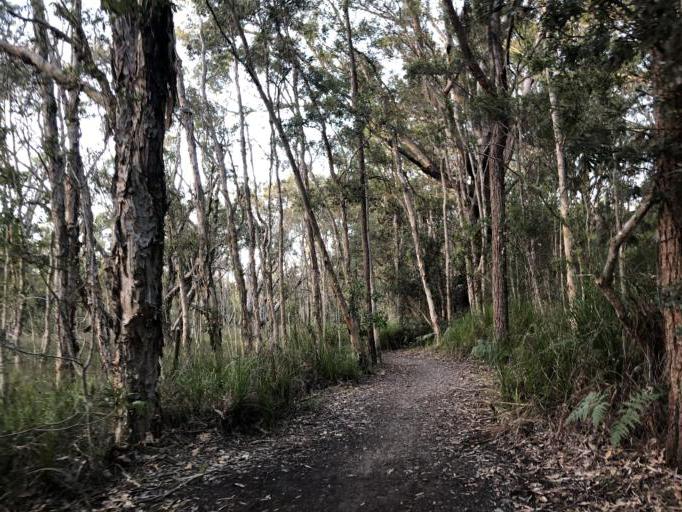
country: AU
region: New South Wales
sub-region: Coffs Harbour
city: Coffs Harbour
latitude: -30.3019
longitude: 153.1314
